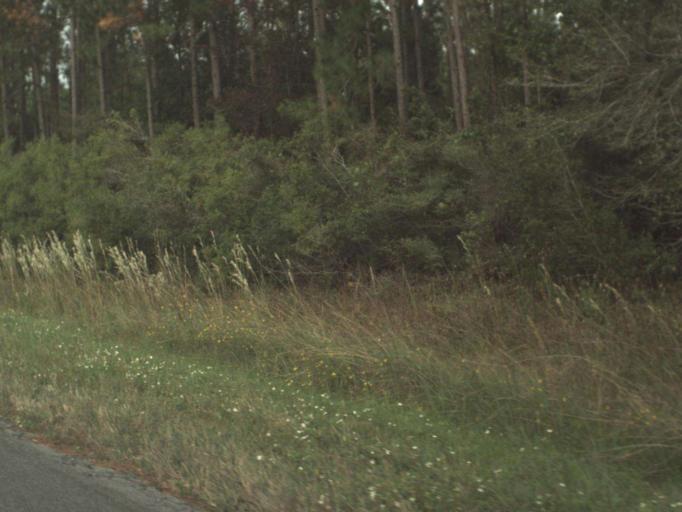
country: US
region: Florida
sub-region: Franklin County
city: Carrabelle
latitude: 29.9836
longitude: -84.5012
